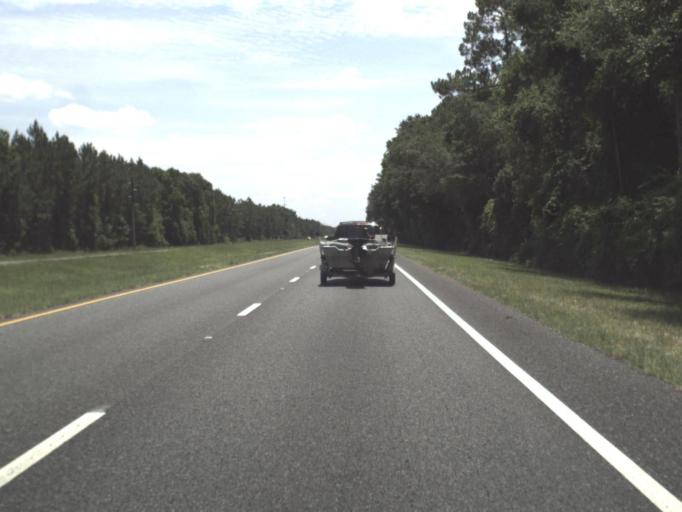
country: US
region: Florida
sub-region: Dixie County
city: Cross City
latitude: 29.6569
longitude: -83.1858
